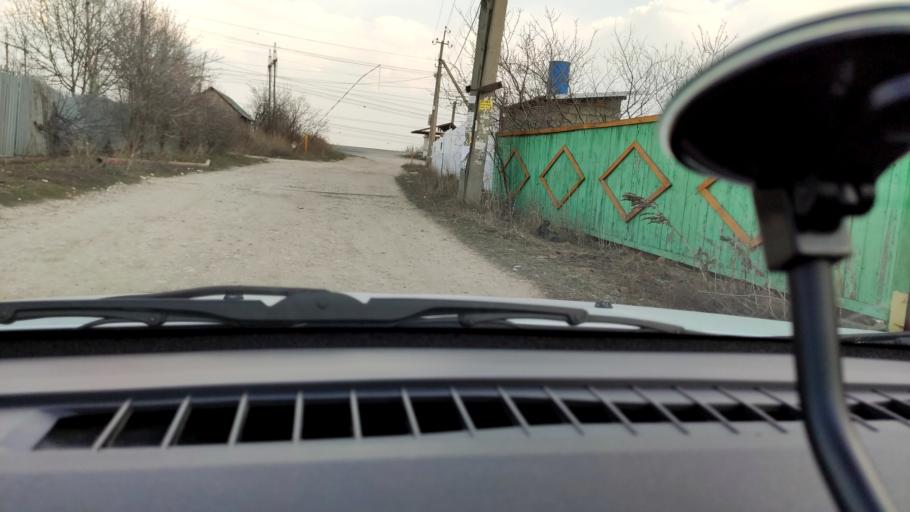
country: RU
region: Samara
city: Smyshlyayevka
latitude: 53.0910
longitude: 50.3958
